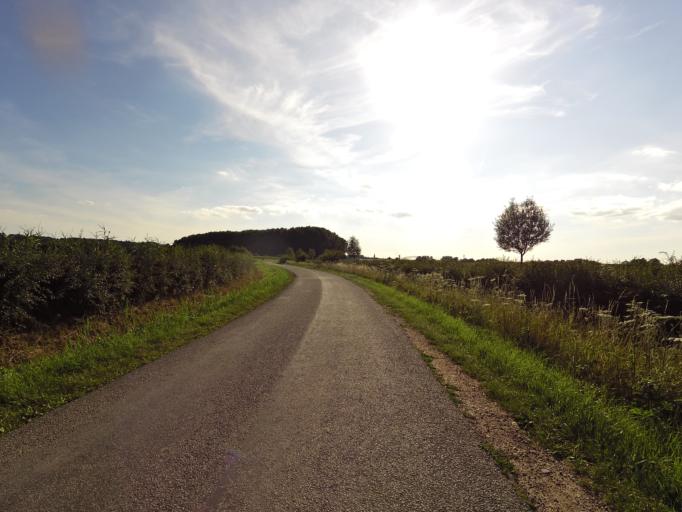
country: NL
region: Gelderland
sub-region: Gemeente Groesbeek
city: Berg en Dal
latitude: 51.8527
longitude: 5.9035
